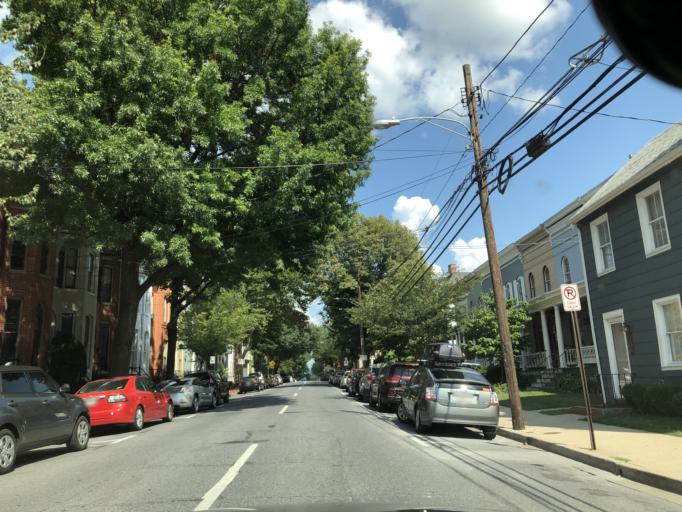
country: US
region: Maryland
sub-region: Frederick County
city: Frederick
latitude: 39.4177
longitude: -77.4083
